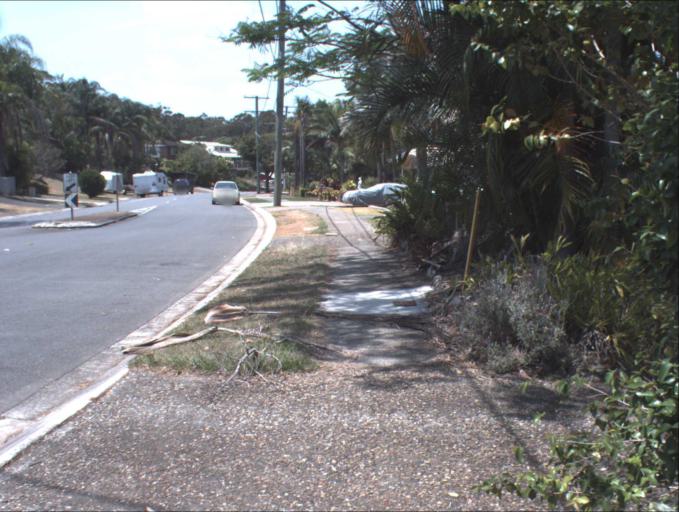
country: AU
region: Queensland
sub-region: Logan
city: Slacks Creek
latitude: -27.6615
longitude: 153.1914
